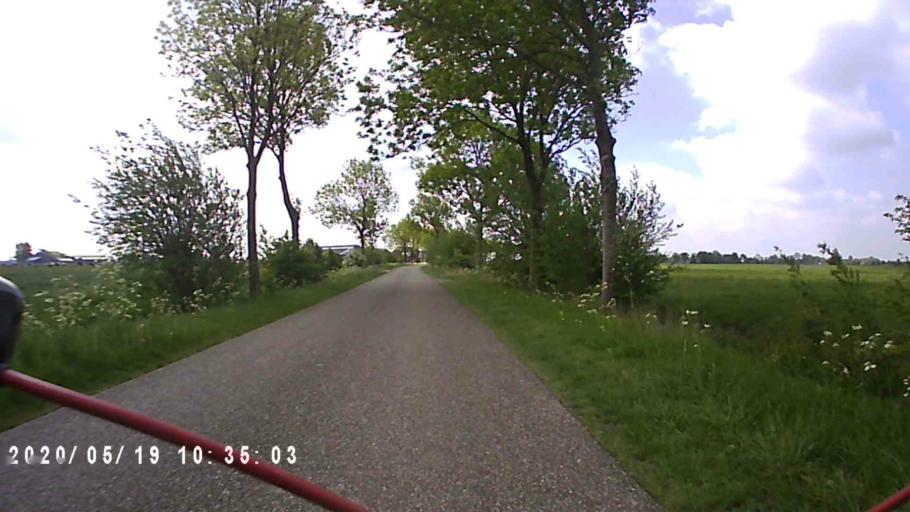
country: NL
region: Friesland
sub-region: Gemeente Kollumerland en Nieuwkruisland
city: Kollum
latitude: 53.2825
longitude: 6.1849
